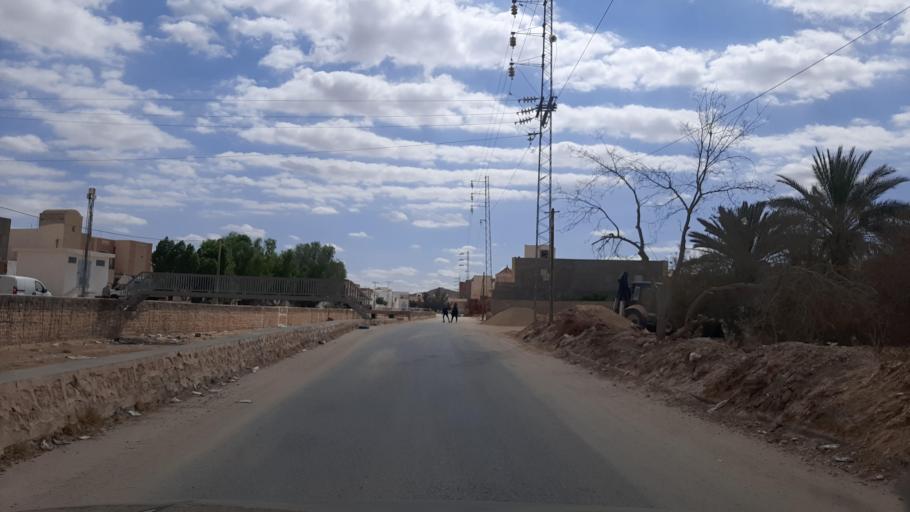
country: TN
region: Tataouine
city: Tataouine
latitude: 32.9310
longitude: 10.4557
